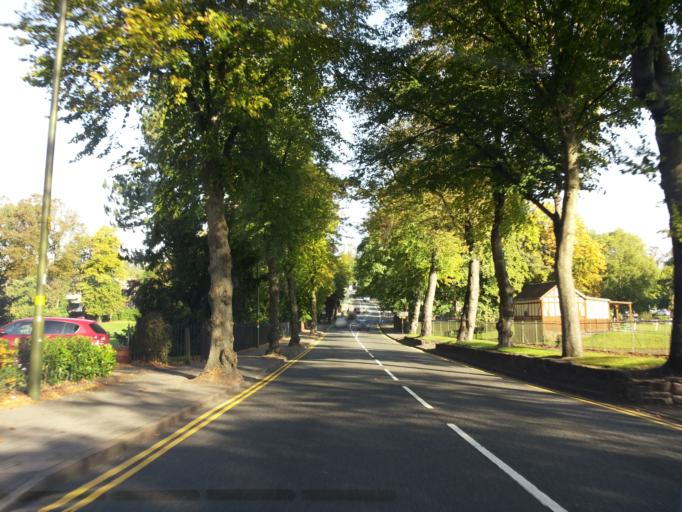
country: GB
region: England
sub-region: City and Borough of Birmingham
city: Bartley Green
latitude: 52.4269
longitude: -1.9354
